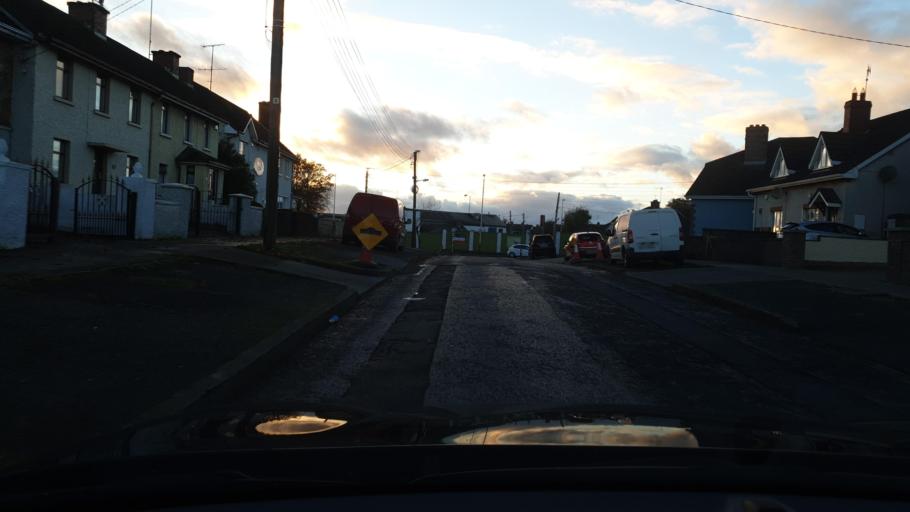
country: IE
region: Leinster
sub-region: Lu
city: Drogheda
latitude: 53.7202
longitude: -6.3551
